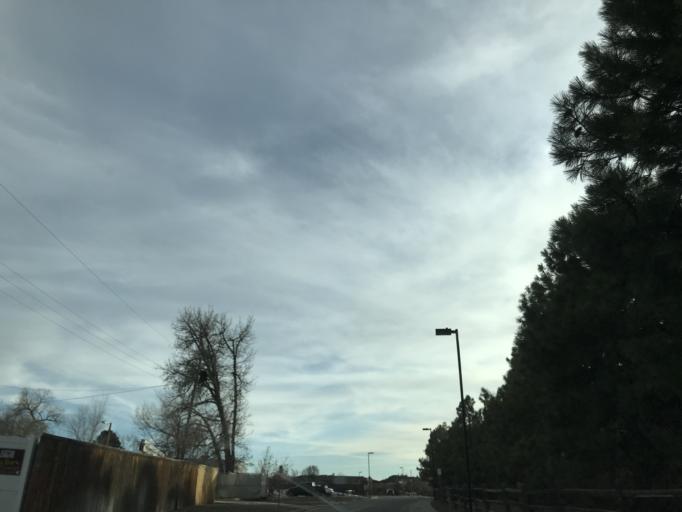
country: US
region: Colorado
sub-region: Arapahoe County
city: Littleton
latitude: 39.6035
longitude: -105.0214
